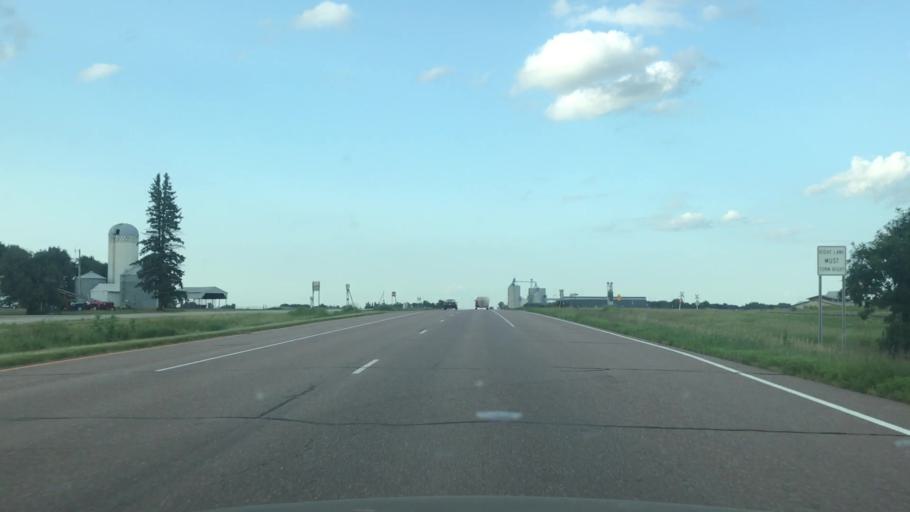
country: US
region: Minnesota
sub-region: Nobles County
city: Worthington
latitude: 43.6878
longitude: -95.4881
